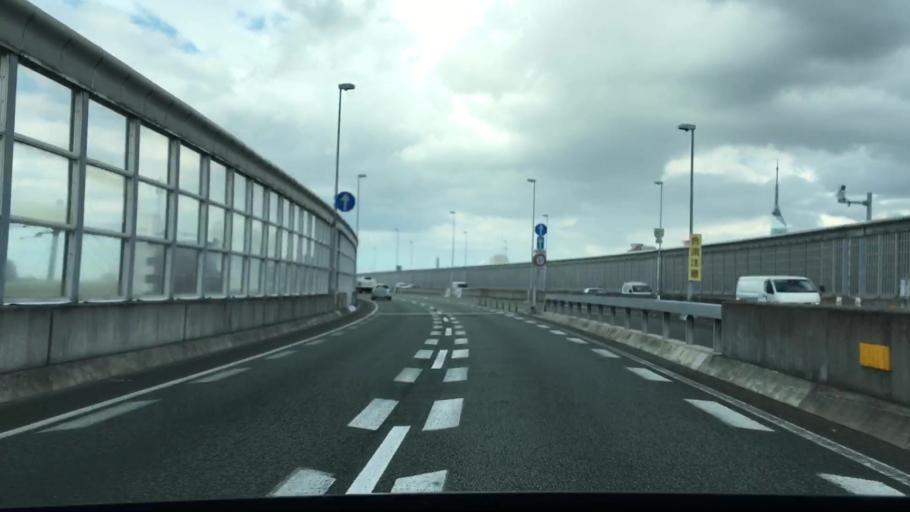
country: JP
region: Fukuoka
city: Fukuoka-shi
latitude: 33.5844
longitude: 130.3401
